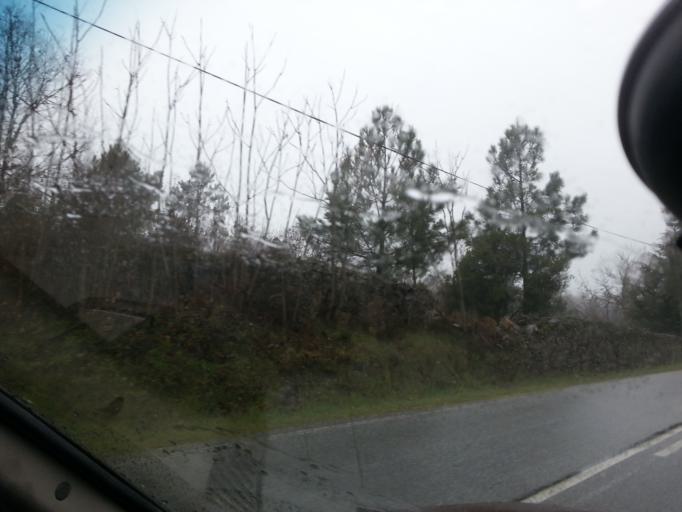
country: PT
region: Viseu
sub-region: Mangualde
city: Mangualde
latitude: 40.6061
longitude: -7.7155
